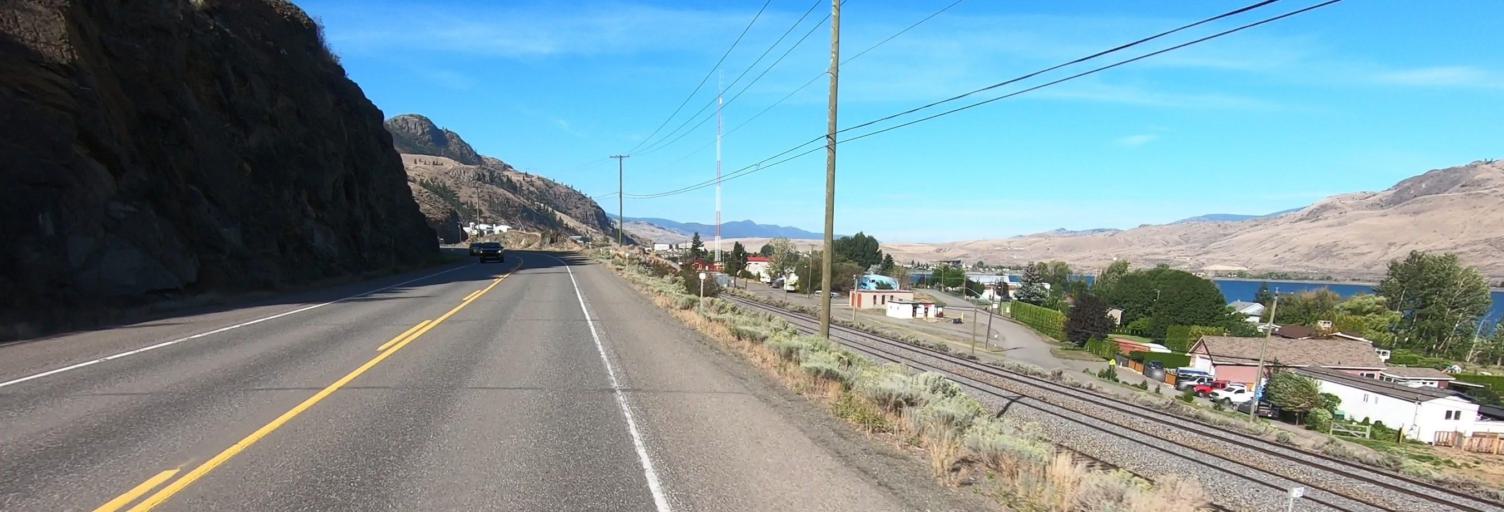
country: CA
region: British Columbia
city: Logan Lake
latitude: 50.7540
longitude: -120.8384
